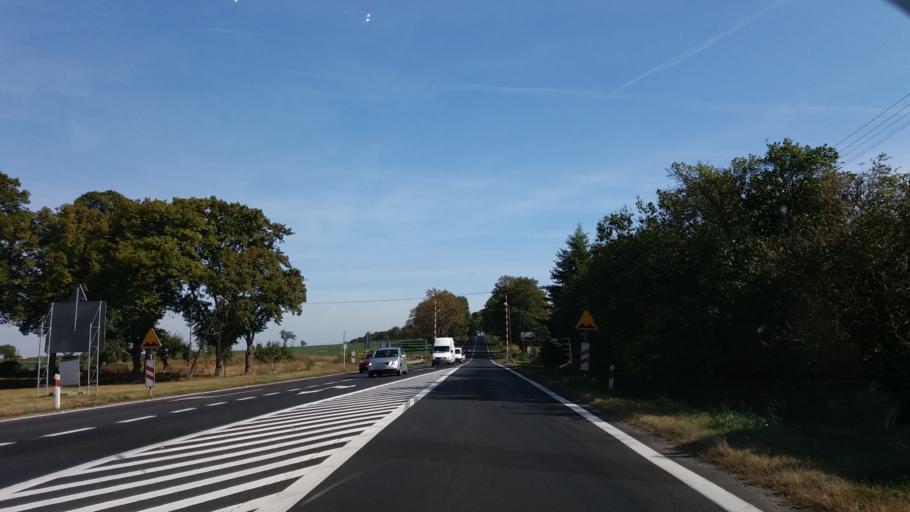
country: PL
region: Greater Poland Voivodeship
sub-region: Powiat miedzychodzki
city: Miedzychod
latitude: 52.5651
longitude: 15.8983
